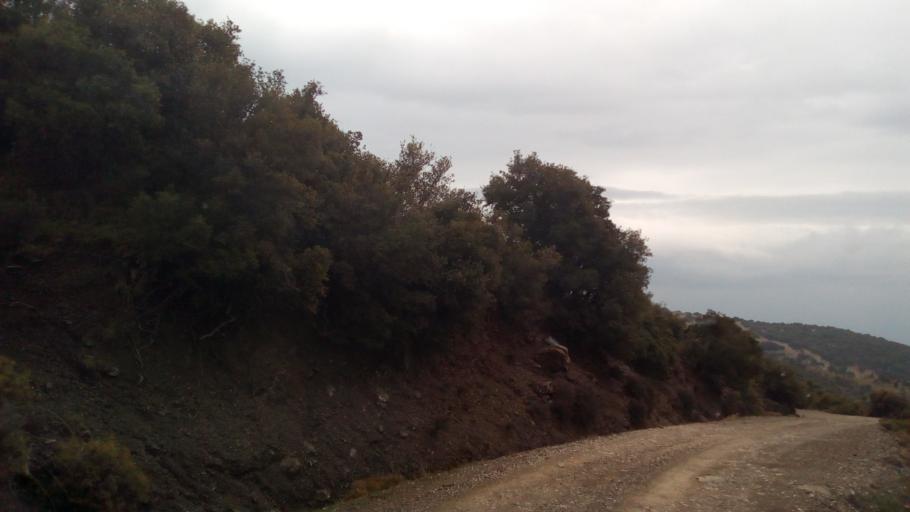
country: GR
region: West Greece
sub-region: Nomos Achaias
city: Selianitika
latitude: 38.4103
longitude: 22.0896
